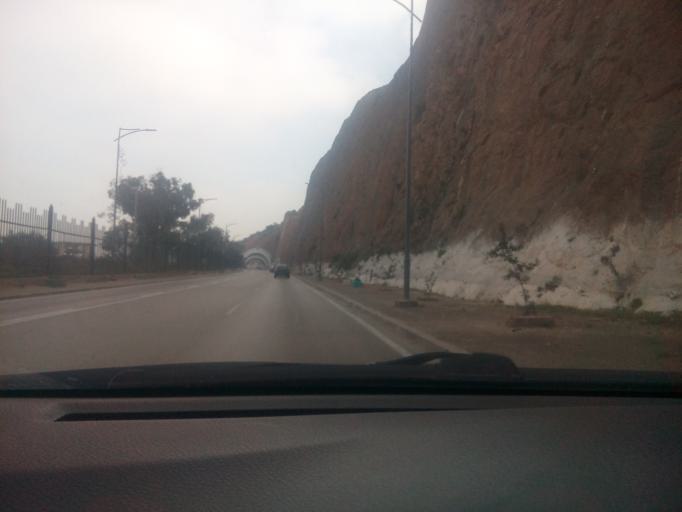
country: DZ
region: Oran
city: Mers el Kebir
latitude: 35.7121
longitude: -0.6780
